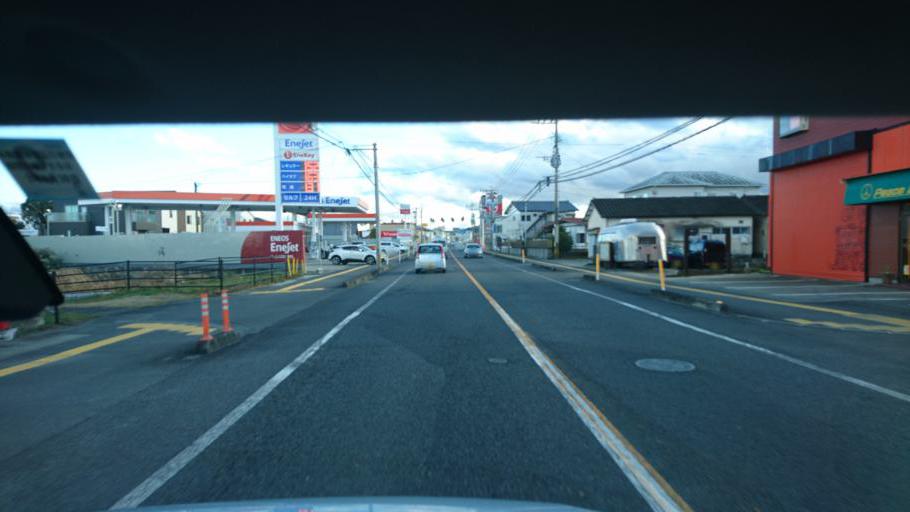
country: JP
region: Miyazaki
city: Miyazaki-shi
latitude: 31.8733
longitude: 131.4314
